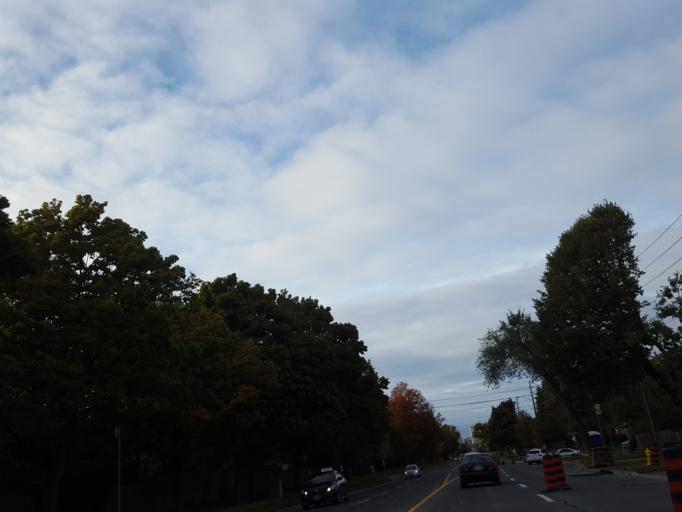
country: CA
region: Ontario
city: Scarborough
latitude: 43.7817
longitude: -79.3093
